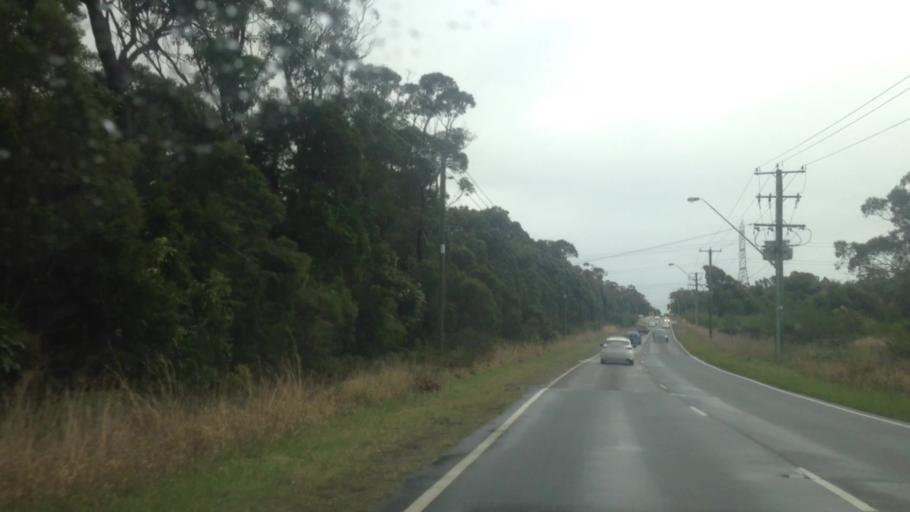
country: AU
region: New South Wales
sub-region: Wyong Shire
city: Charmhaven
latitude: -33.1613
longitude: 151.4784
